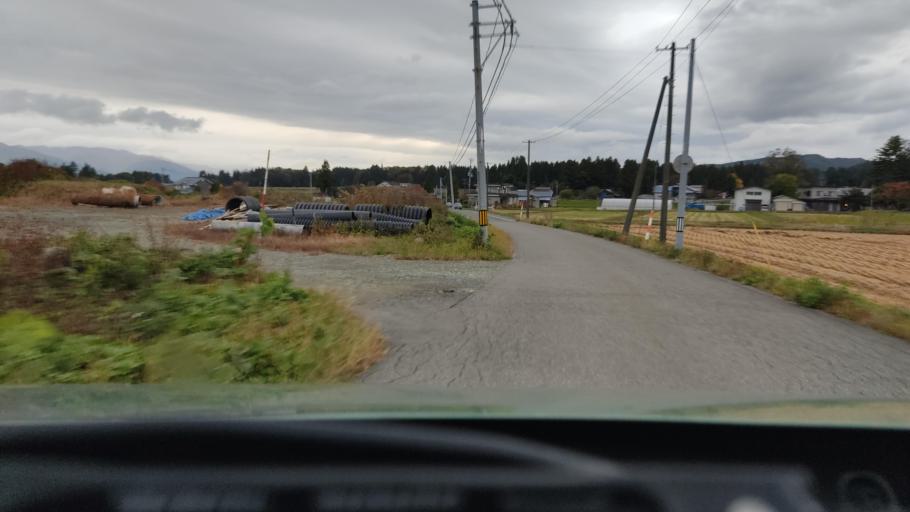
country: JP
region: Akita
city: Kakunodatemachi
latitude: 39.5659
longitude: 140.6112
